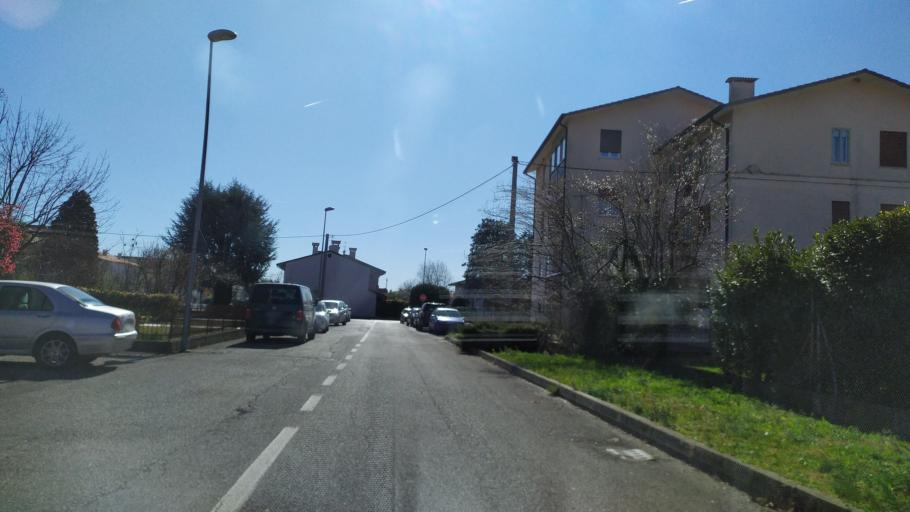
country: IT
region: Veneto
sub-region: Provincia di Vicenza
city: Breganze
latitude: 45.7030
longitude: 11.5673
